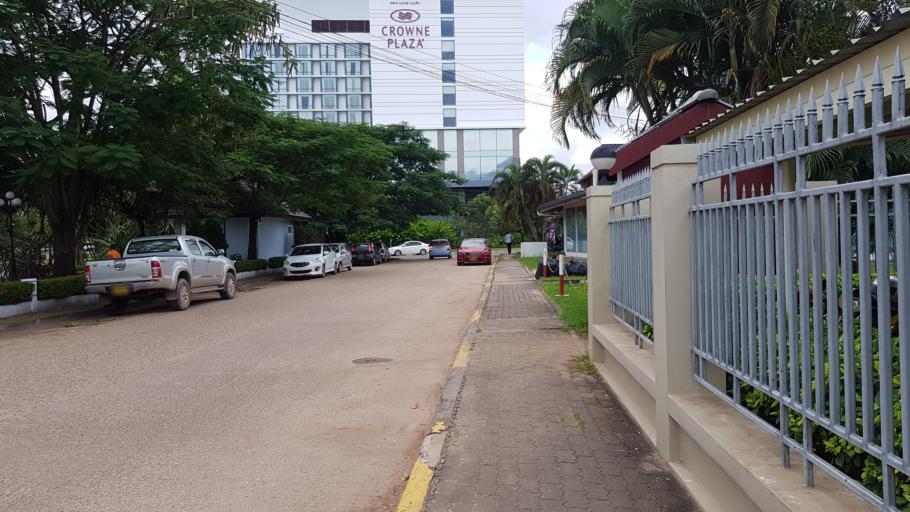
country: LA
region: Vientiane
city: Vientiane
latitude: 17.9684
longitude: 102.5967
